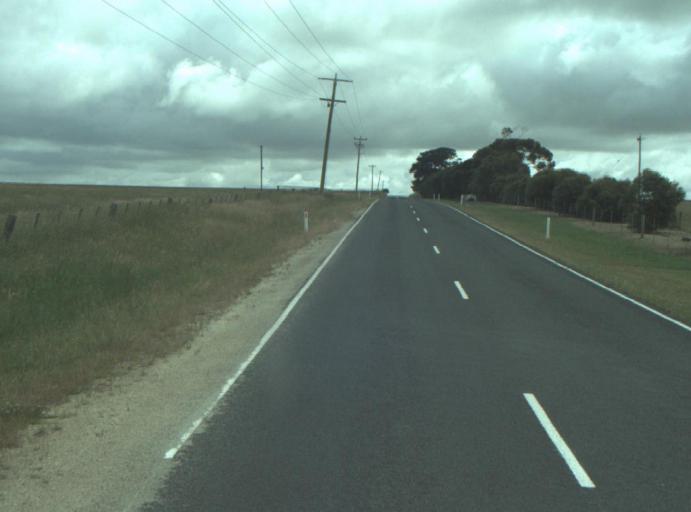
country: AU
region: Victoria
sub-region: Greater Geelong
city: Wandana Heights
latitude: -38.1876
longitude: 144.2688
